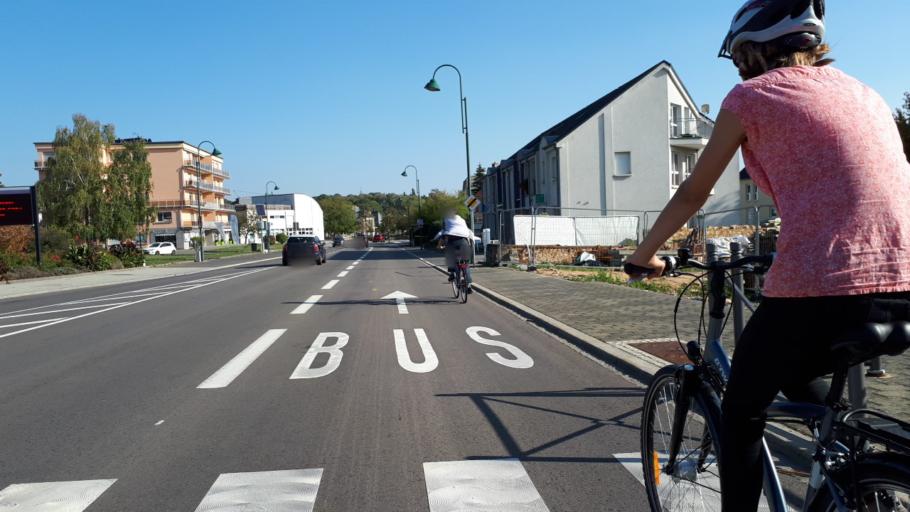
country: LU
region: Luxembourg
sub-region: Canton de Capellen
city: Mamer
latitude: 49.6281
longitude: 6.0302
